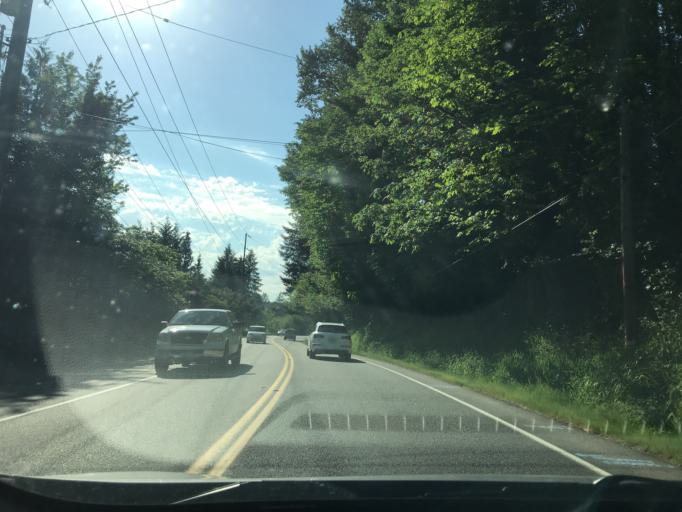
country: US
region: Washington
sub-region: King County
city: Mirrormont
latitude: 47.4617
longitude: -122.0101
